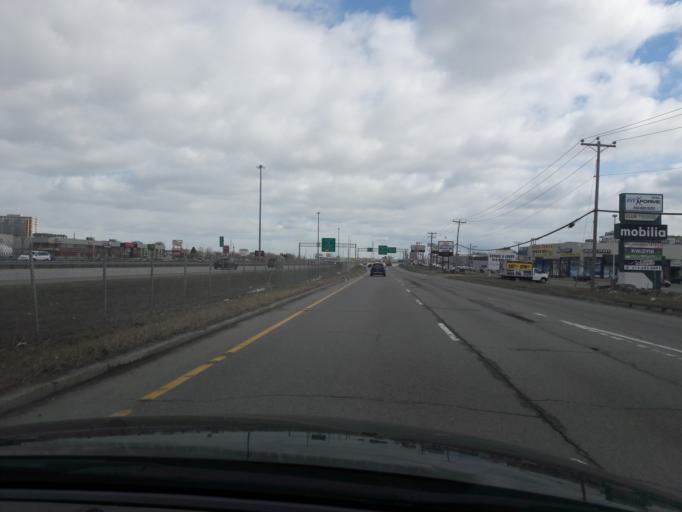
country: CA
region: Quebec
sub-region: Laurentides
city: Rosemere
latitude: 45.5645
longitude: -73.7740
